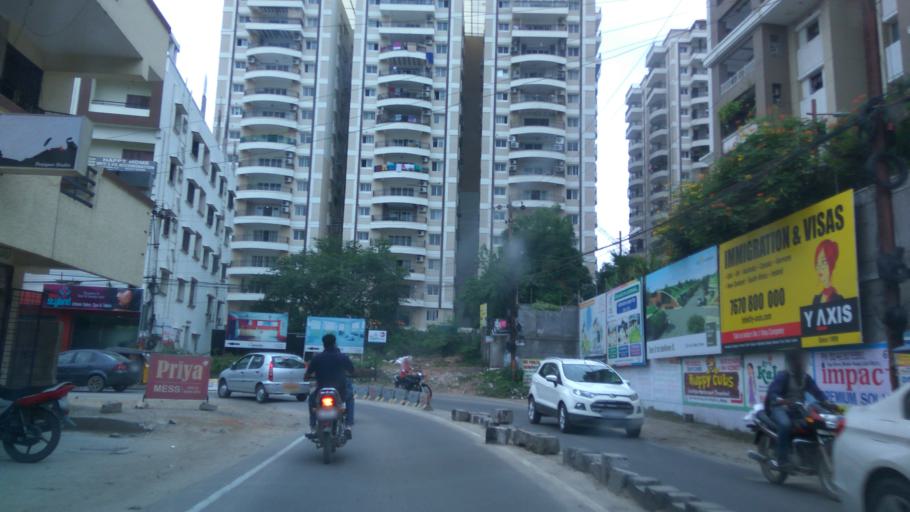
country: IN
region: Telangana
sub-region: Rangareddi
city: Kukatpalli
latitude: 17.4386
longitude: 78.3904
